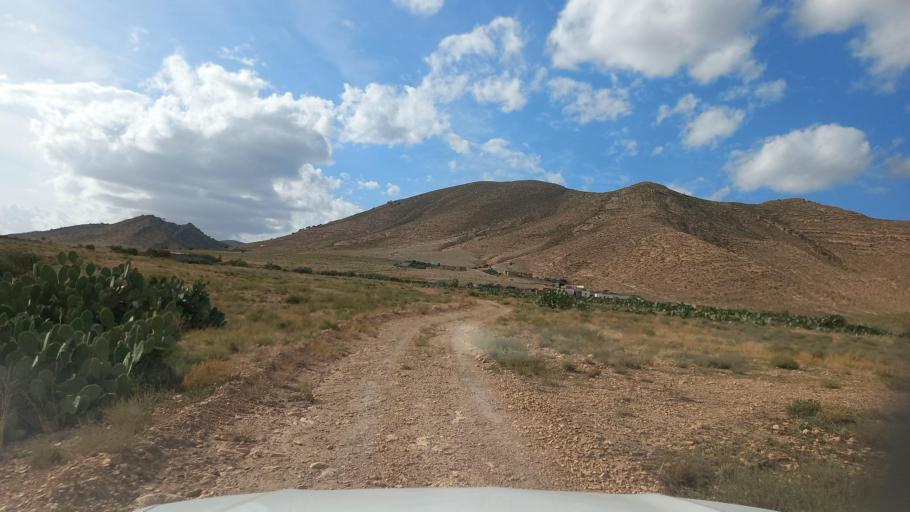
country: TN
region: Al Qasrayn
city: Sbiba
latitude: 35.4551
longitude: 9.0712
